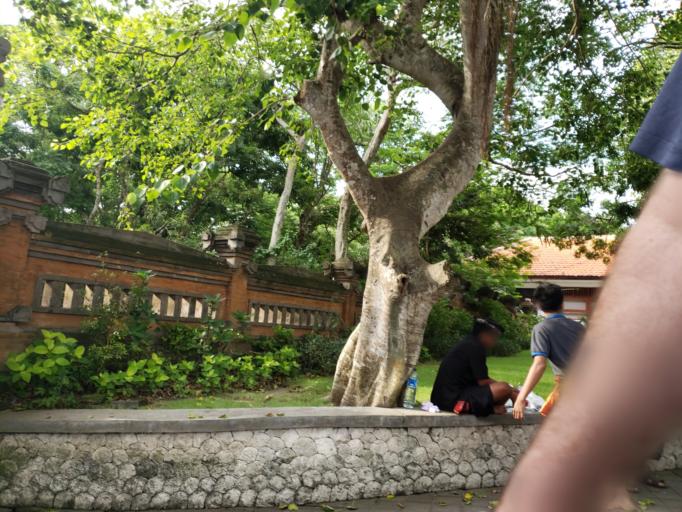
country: ID
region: Bali
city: Pecatu
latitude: -8.8297
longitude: 115.0864
